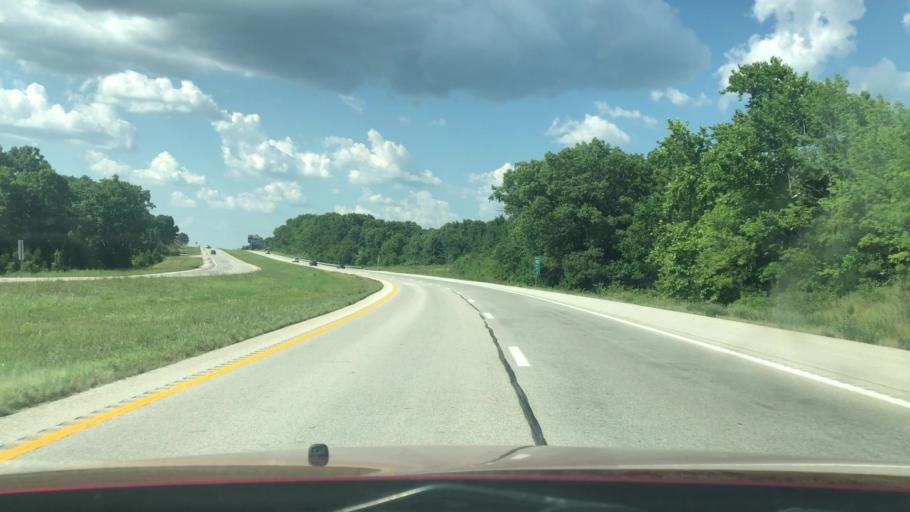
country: US
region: Missouri
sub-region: Christian County
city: Ozark
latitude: 36.9288
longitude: -93.2325
